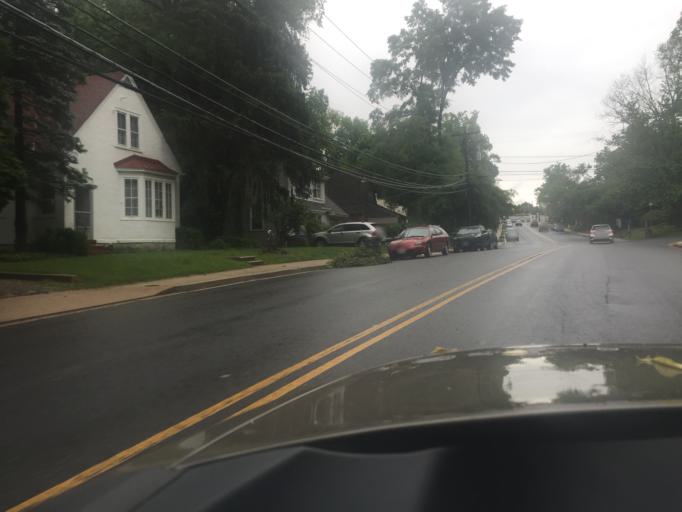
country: US
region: Virginia
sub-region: Arlington County
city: Arlington
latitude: 38.8999
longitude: -77.1091
